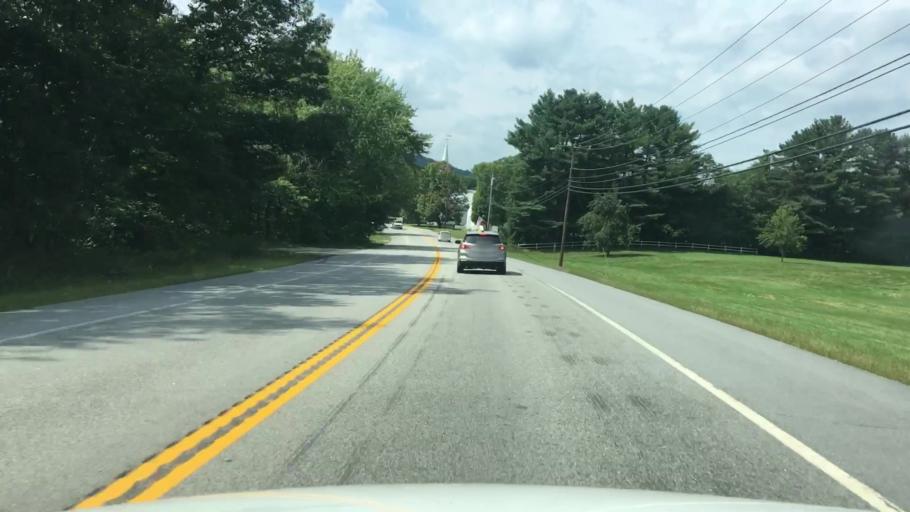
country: US
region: Maine
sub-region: Oxford County
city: Rumford
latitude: 44.5123
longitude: -70.6108
